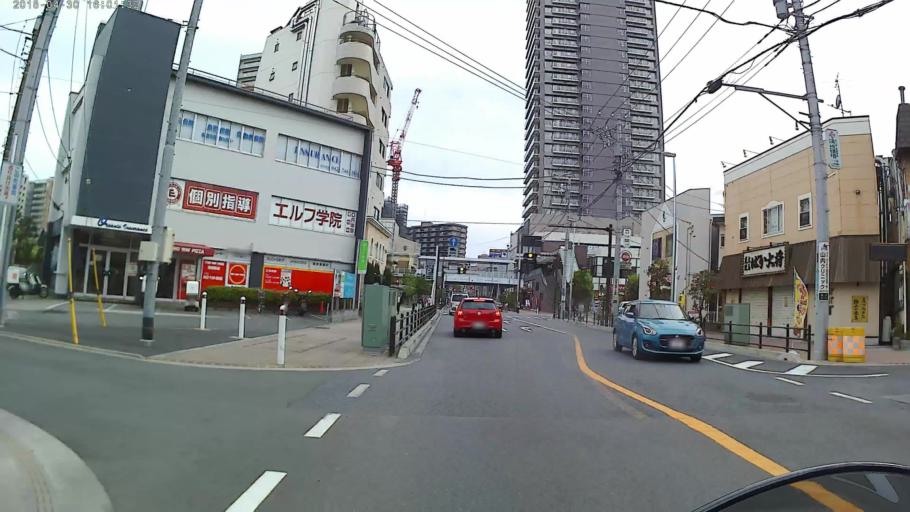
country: JP
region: Tokyo
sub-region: Machida-shi
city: Machida
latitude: 35.5165
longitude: 139.4221
